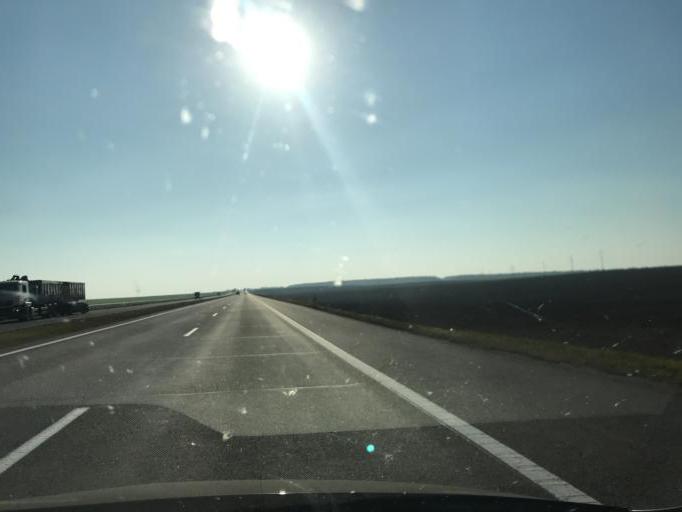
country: BY
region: Grodnenskaya
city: Mir
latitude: 53.4353
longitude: 26.5873
